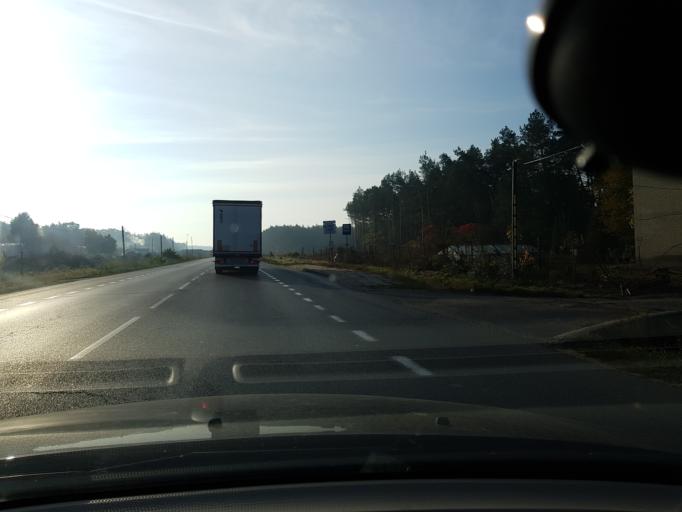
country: PL
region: Masovian Voivodeship
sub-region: Powiat otwocki
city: Otwock
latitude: 52.1596
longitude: 21.3054
